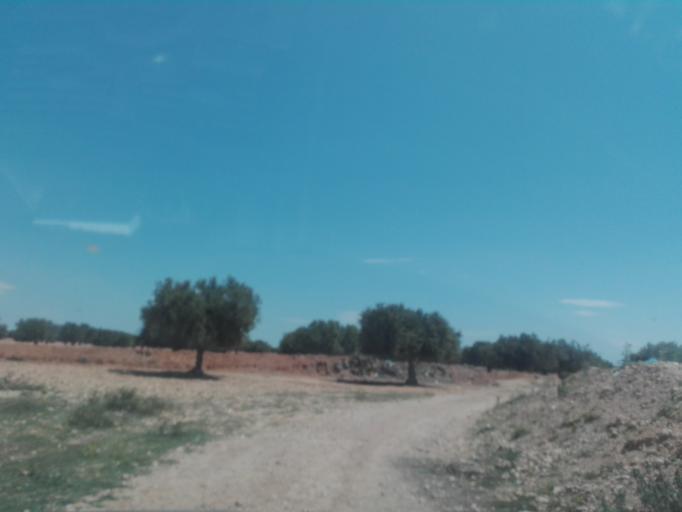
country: TN
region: Safaqis
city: Sfax
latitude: 34.6545
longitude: 10.5868
